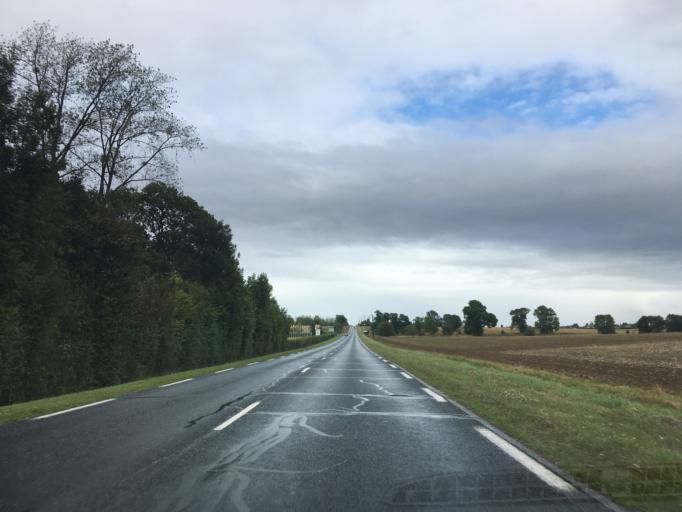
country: FR
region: Haute-Normandie
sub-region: Departement de l'Eure
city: Verneuil-sur-Avre
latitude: 48.7404
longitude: 0.8908
